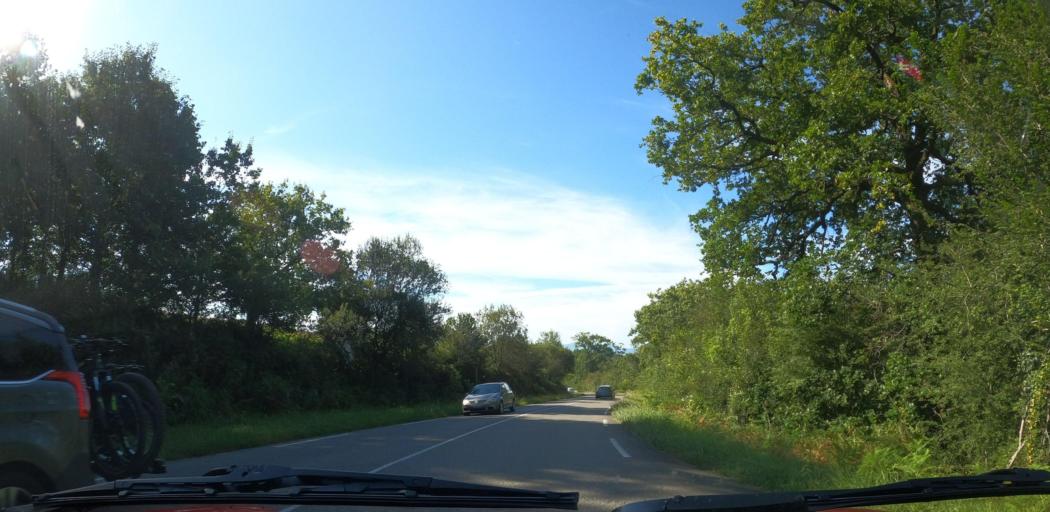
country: FR
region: Aquitaine
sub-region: Departement des Pyrenees-Atlantiques
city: Saint-Pee-sur-Nivelle
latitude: 43.3810
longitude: -1.5393
